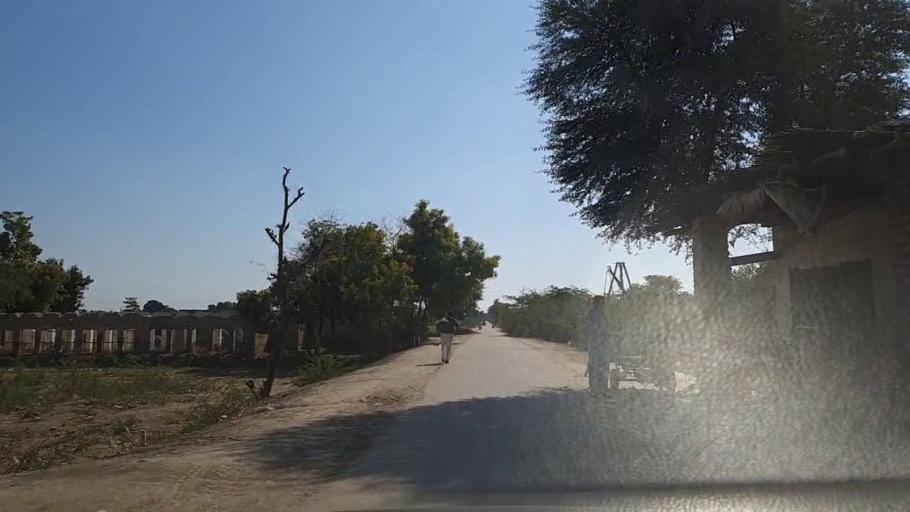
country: PK
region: Sindh
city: Nawabshah
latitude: 26.2450
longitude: 68.4457
